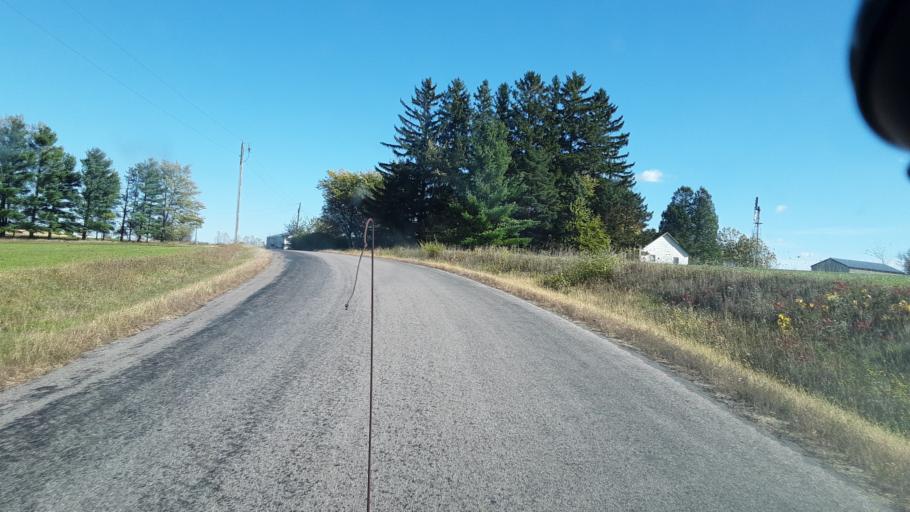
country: US
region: Wisconsin
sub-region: Vernon County
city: Hillsboro
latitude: 43.6852
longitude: -90.4214
